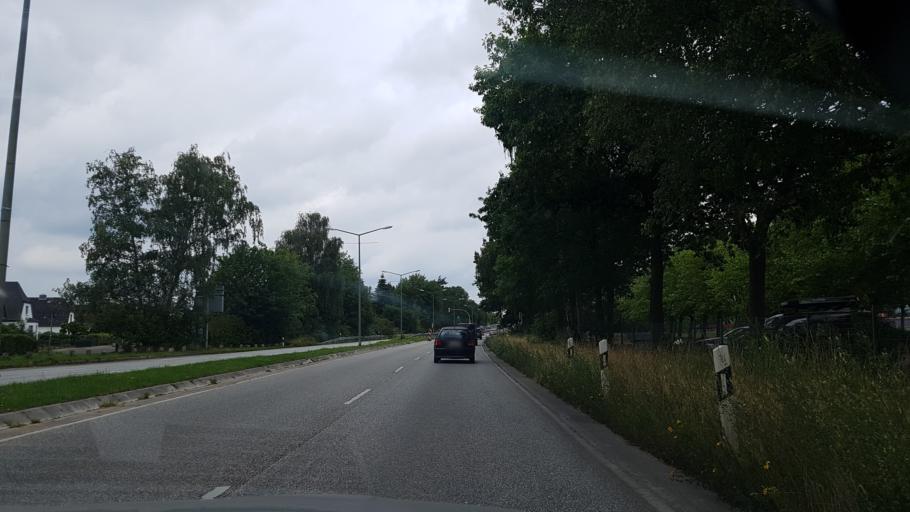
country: DE
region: Schleswig-Holstein
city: Neumunster
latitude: 54.0928
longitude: 9.9741
